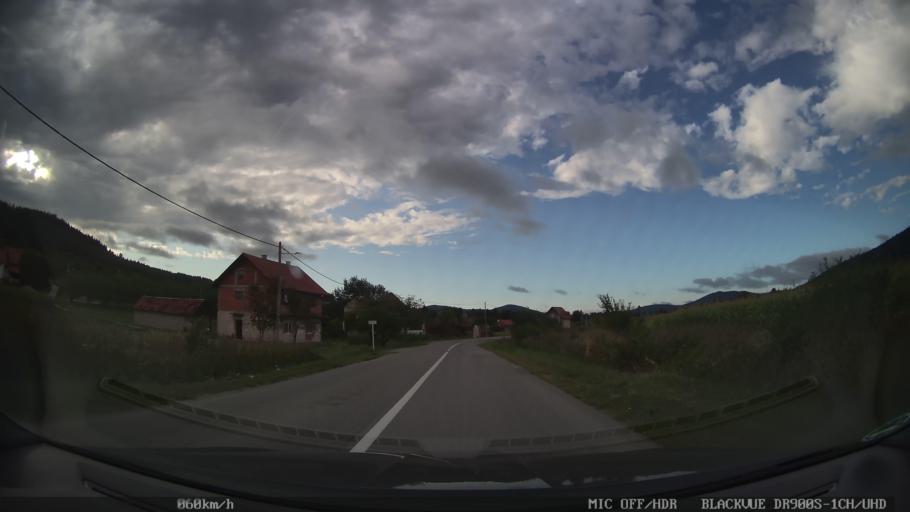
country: HR
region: Karlovacka
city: Plaski
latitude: 44.9864
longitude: 15.4691
